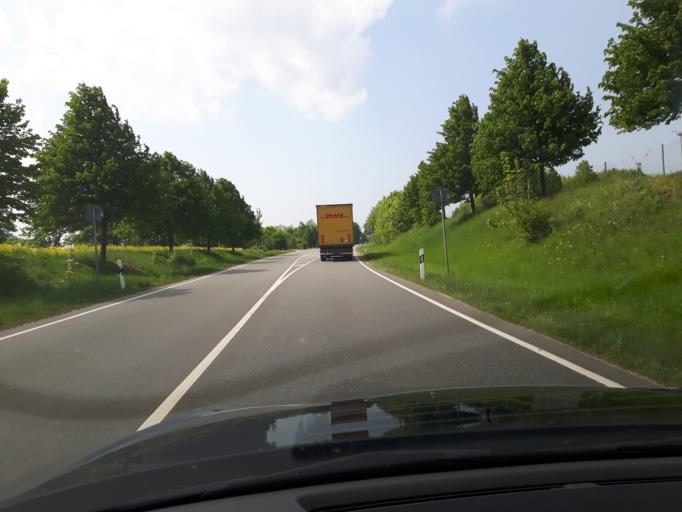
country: DE
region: Mecklenburg-Vorpommern
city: Selmsdorf
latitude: 53.8651
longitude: 10.9068
